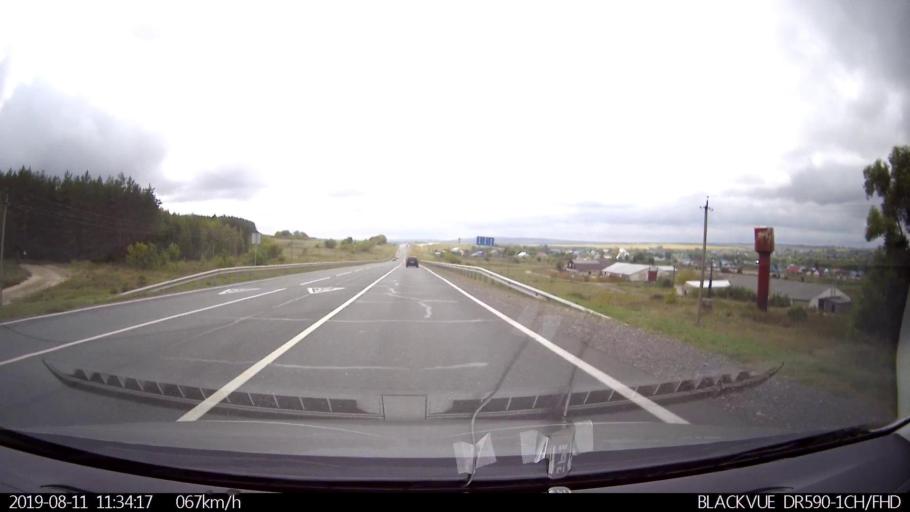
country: RU
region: Ulyanovsk
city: Silikatnyy
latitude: 54.0198
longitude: 48.2155
